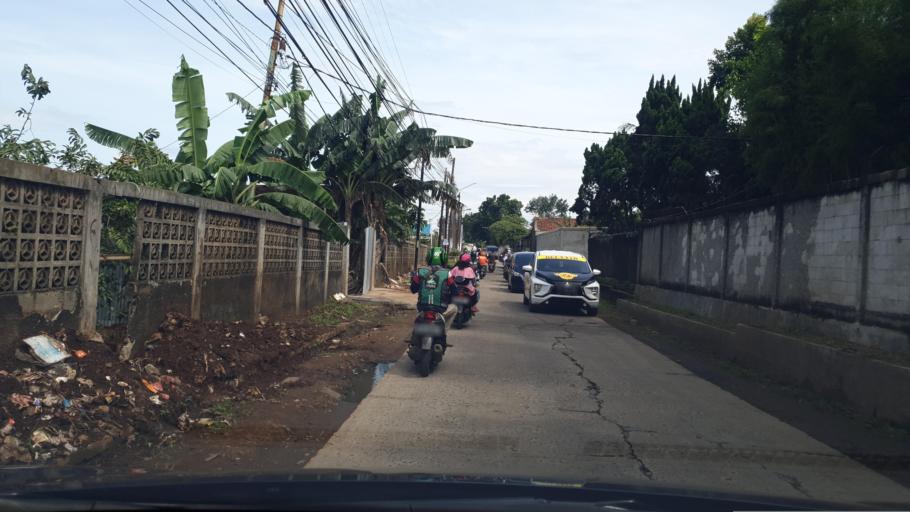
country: ID
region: West Java
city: Sawangan
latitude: -6.4076
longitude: 106.7702
